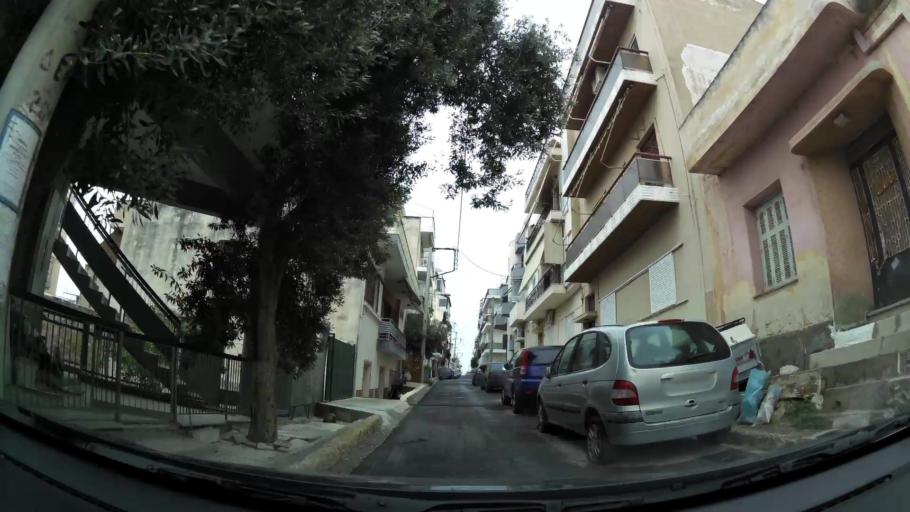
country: GR
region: Attica
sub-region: Nomos Piraios
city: Nikaia
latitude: 37.9600
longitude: 23.6454
